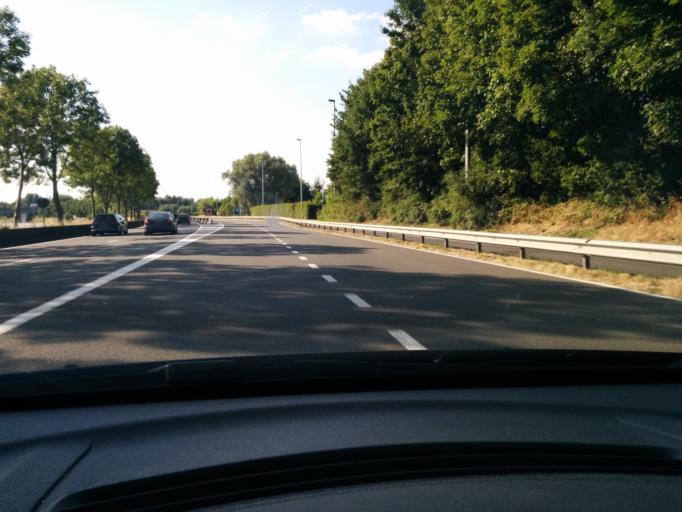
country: BE
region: Flanders
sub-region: Provincie Oost-Vlaanderen
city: Gent
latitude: 51.0297
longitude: 3.7017
